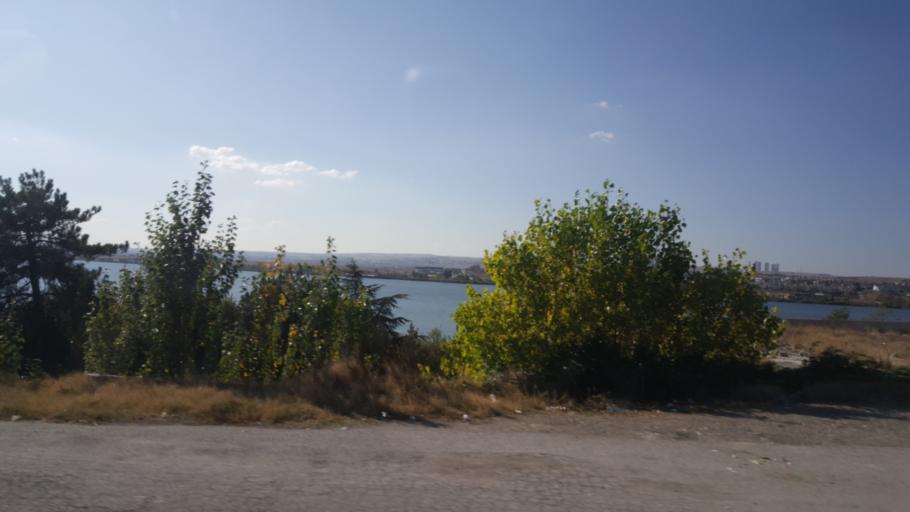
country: TR
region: Ankara
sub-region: Goelbasi
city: Golbasi
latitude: 39.7799
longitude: 32.8043
